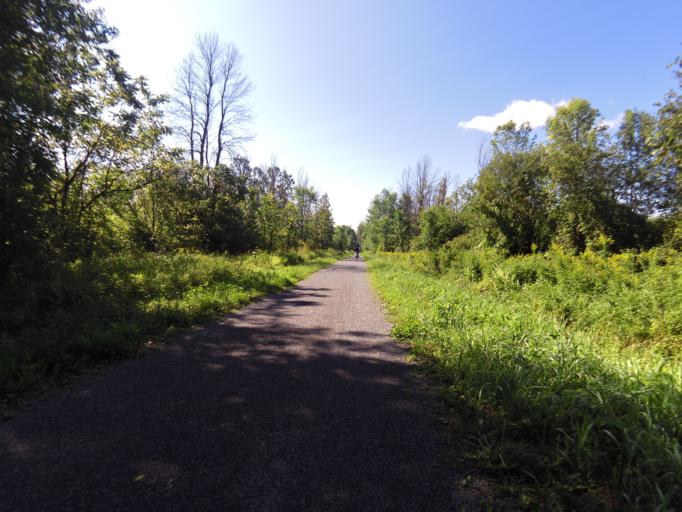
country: CA
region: Ontario
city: Ottawa
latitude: 45.2033
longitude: -75.6242
